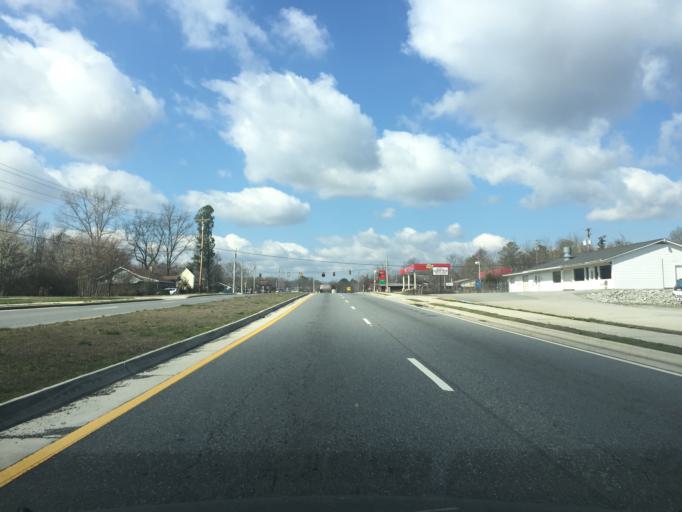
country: US
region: Georgia
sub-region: Catoosa County
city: Fort Oglethorpe
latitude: 34.9574
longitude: -85.2186
